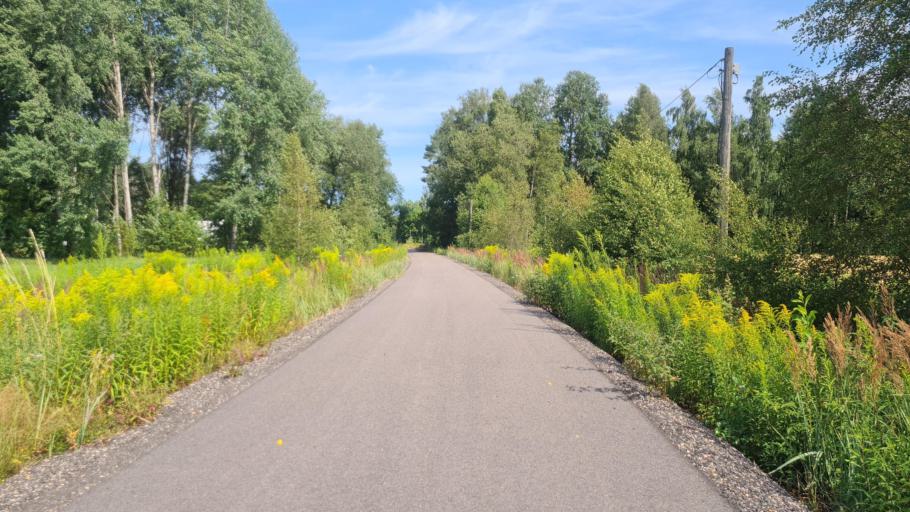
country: SE
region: Kronoberg
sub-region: Ljungby Kommun
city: Lagan
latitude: 56.9055
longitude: 13.9909
